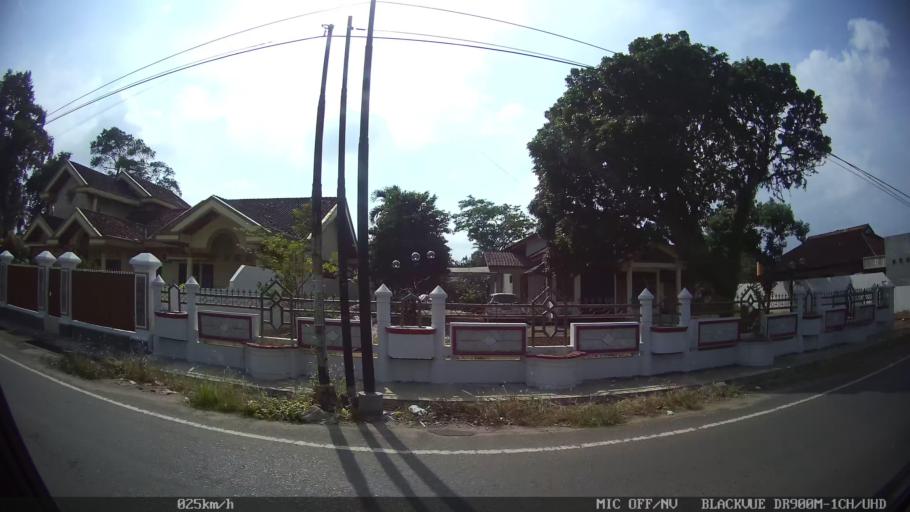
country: ID
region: Lampung
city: Kedaton
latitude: -5.3724
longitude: 105.2543
